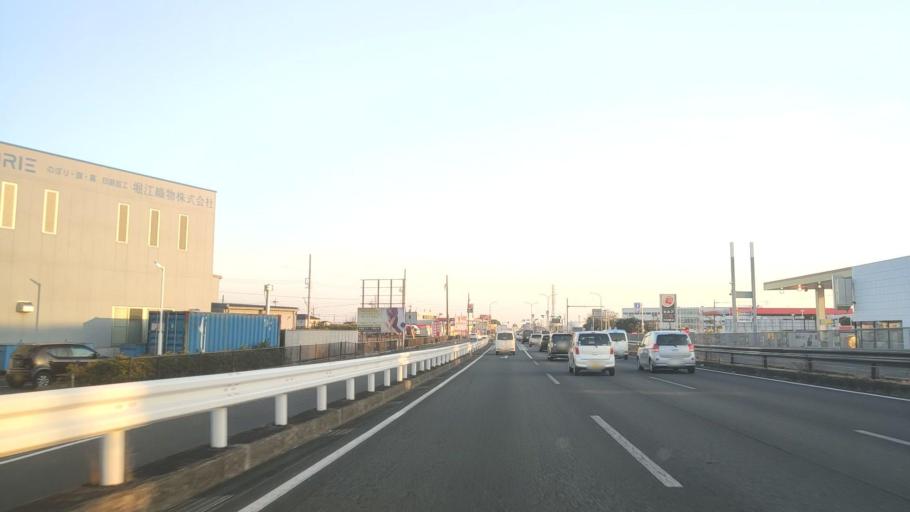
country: JP
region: Aichi
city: Kuroda
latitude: 35.3385
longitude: 136.7991
